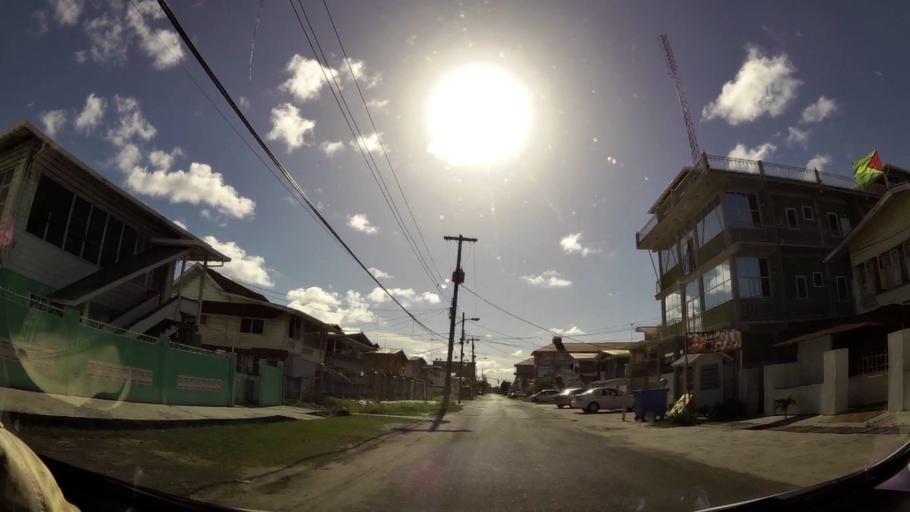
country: GY
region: Demerara-Mahaica
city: Georgetown
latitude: 6.8121
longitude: -58.1374
